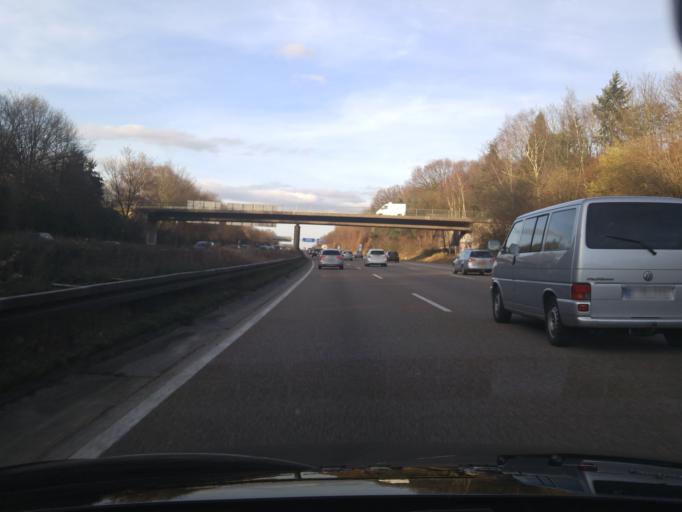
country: DE
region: North Rhine-Westphalia
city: Leichlingen
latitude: 51.1176
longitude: 6.9847
